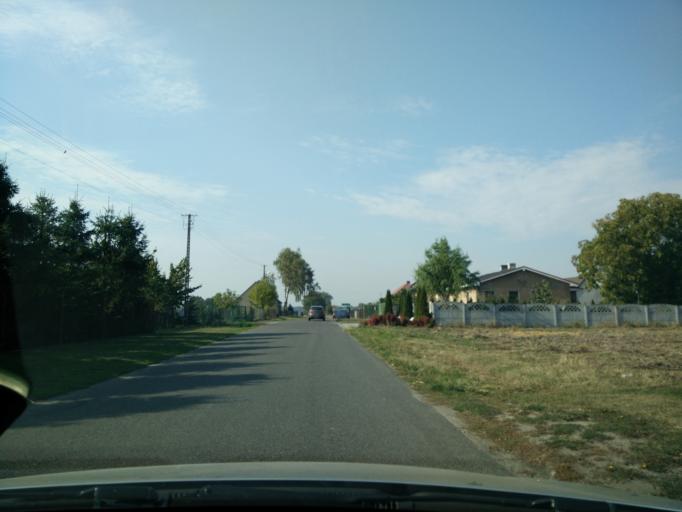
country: PL
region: Greater Poland Voivodeship
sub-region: Powiat sredzki
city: Dominowo
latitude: 52.3171
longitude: 17.3243
